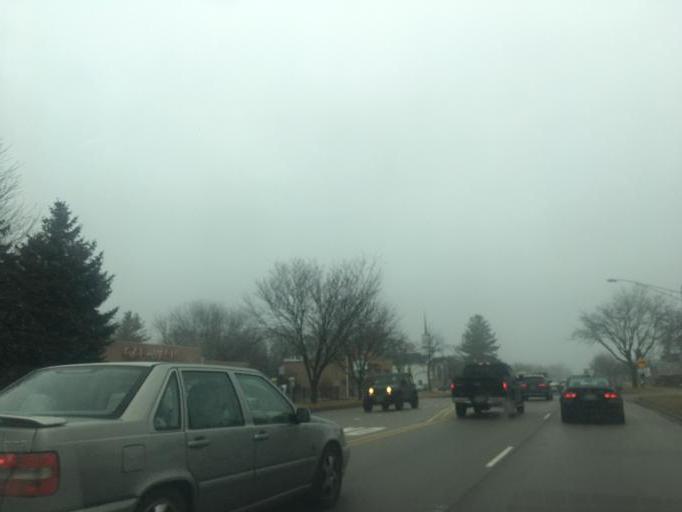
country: US
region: Illinois
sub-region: DuPage County
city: Lisle
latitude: 41.8013
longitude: -88.0743
